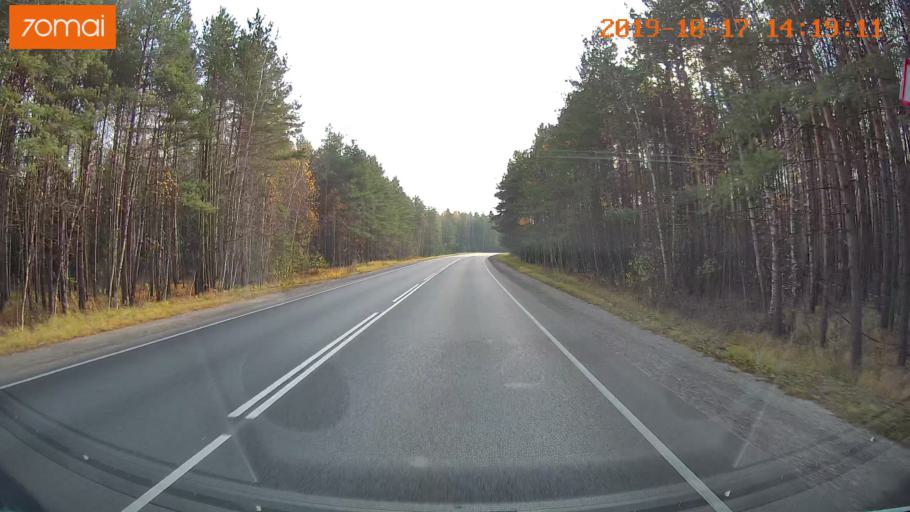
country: RU
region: Rjazan
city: Spas-Klepiki
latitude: 55.0532
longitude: 40.0237
